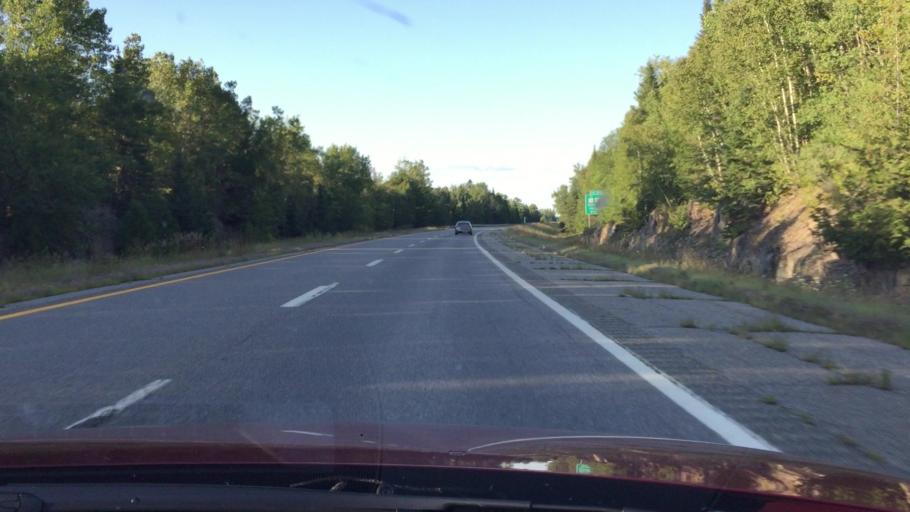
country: US
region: Maine
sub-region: Penobscot County
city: Patten
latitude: 45.8426
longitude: -68.4322
